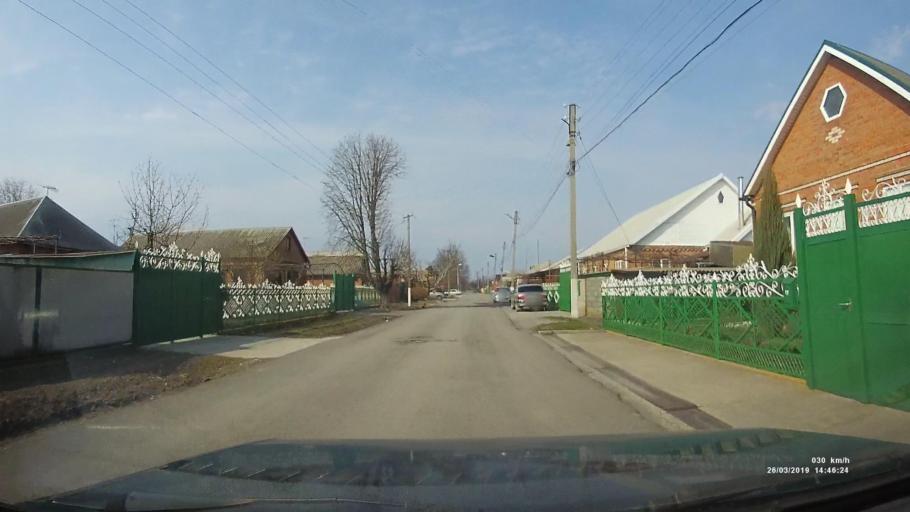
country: RU
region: Rostov
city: Novobessergenovka
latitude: 47.1864
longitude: 38.8605
